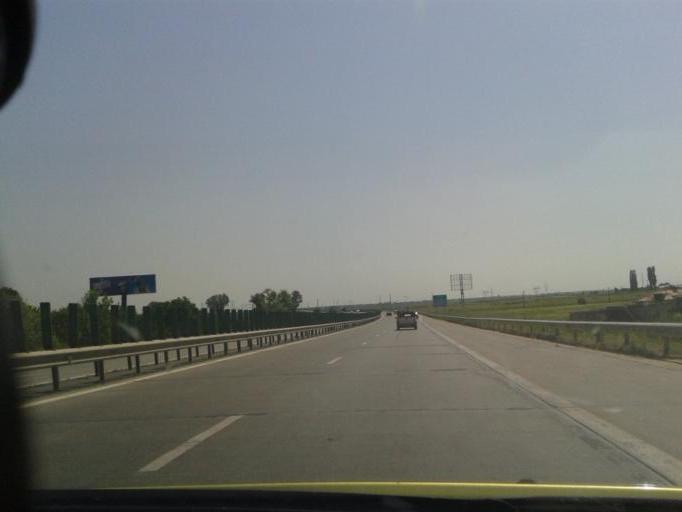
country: RO
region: Ilfov
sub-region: Comuna Cernica
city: Caldararu
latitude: 44.4084
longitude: 26.2656
